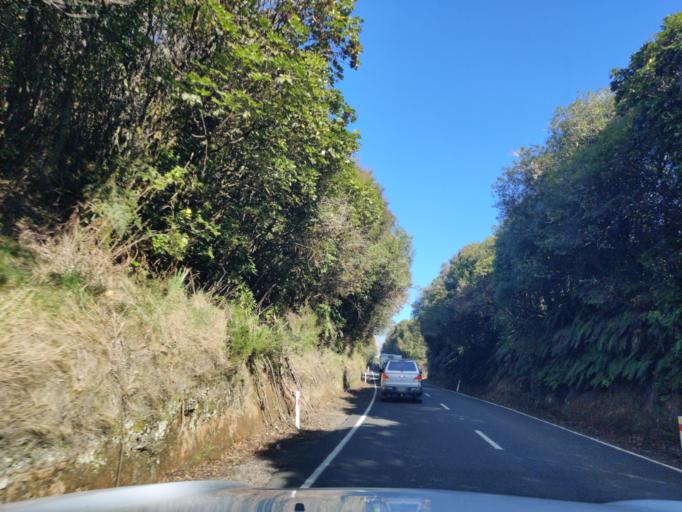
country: NZ
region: Waikato
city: Turangi
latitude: -38.7135
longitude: 175.6637
